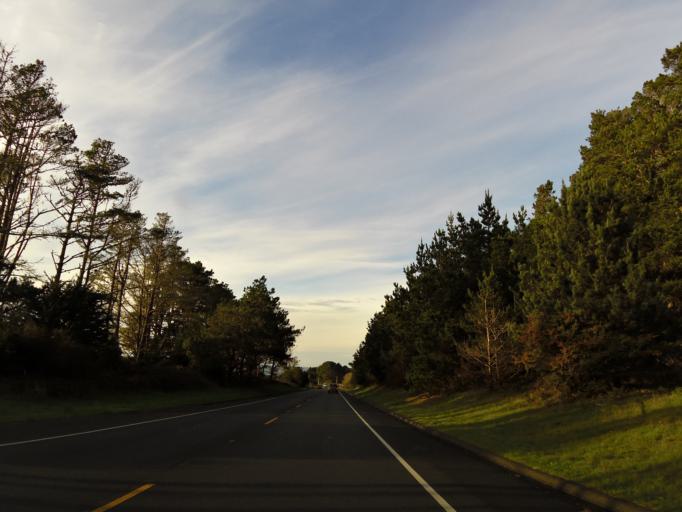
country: US
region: California
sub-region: Mendocino County
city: Fort Bragg
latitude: 39.3687
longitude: -123.8125
